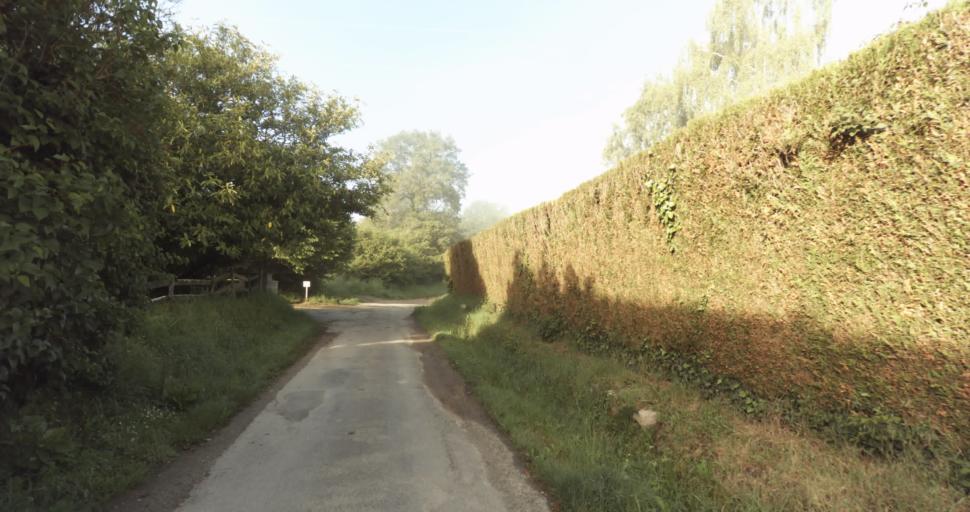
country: FR
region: Limousin
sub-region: Departement de la Haute-Vienne
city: Condat-sur-Vienne
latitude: 45.7811
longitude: 1.2786
